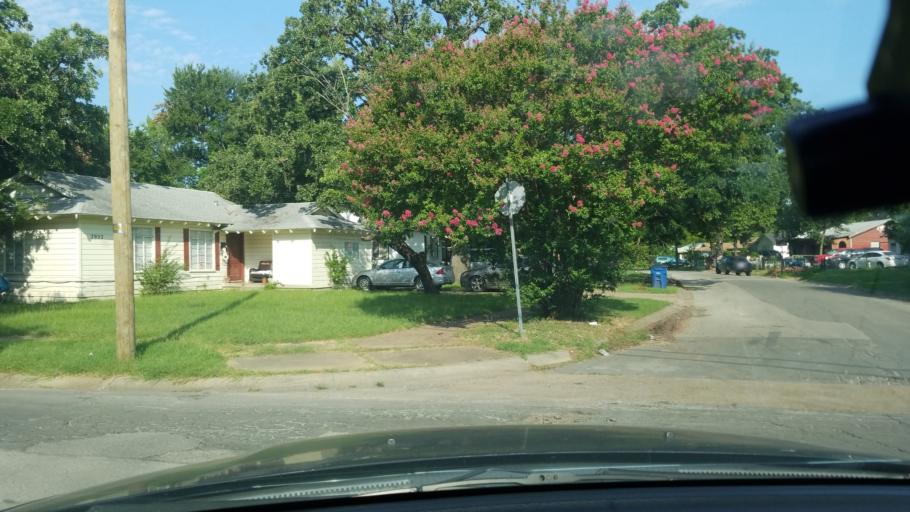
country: US
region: Texas
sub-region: Dallas County
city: Balch Springs
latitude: 32.7208
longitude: -96.6849
